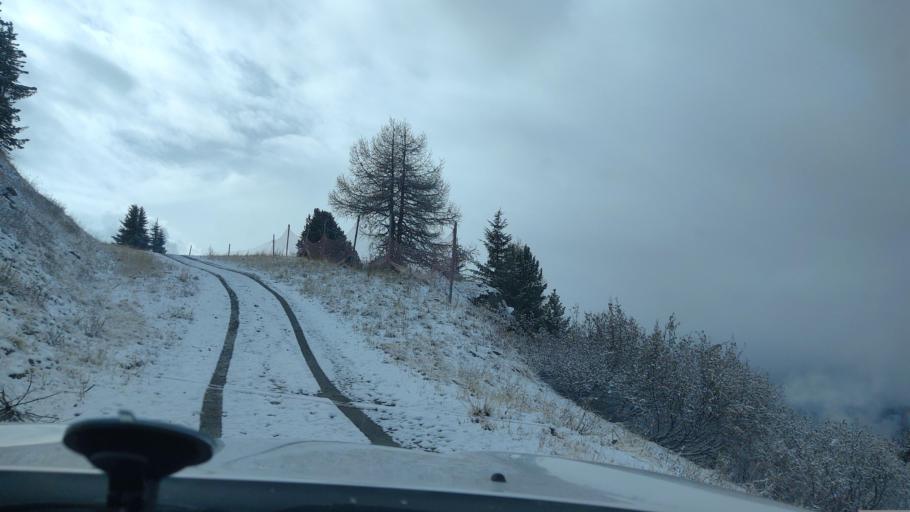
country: FR
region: Rhone-Alpes
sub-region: Departement de la Savoie
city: Seez
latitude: 45.5861
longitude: 6.8031
